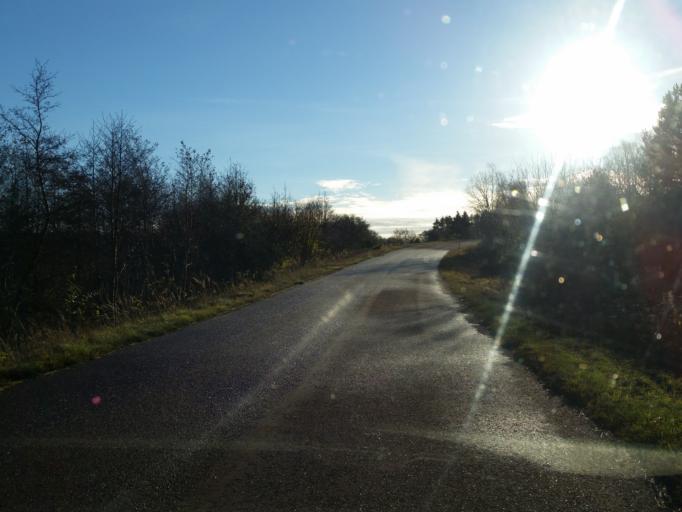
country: AX
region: Alands skaergard
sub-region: Kumlinge
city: Kumlinge
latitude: 60.2116
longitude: 20.7054
